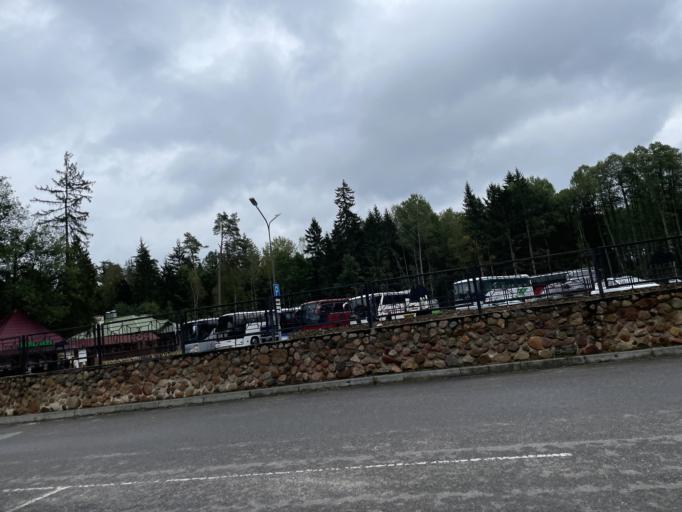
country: BY
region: Brest
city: Kamyanyuki
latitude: 52.5689
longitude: 23.8025
